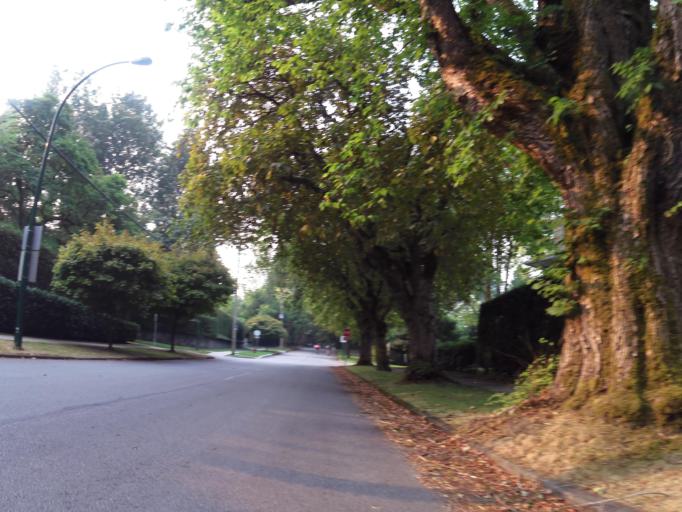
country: CA
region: British Columbia
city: Vancouver
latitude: 49.2533
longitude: -123.1486
